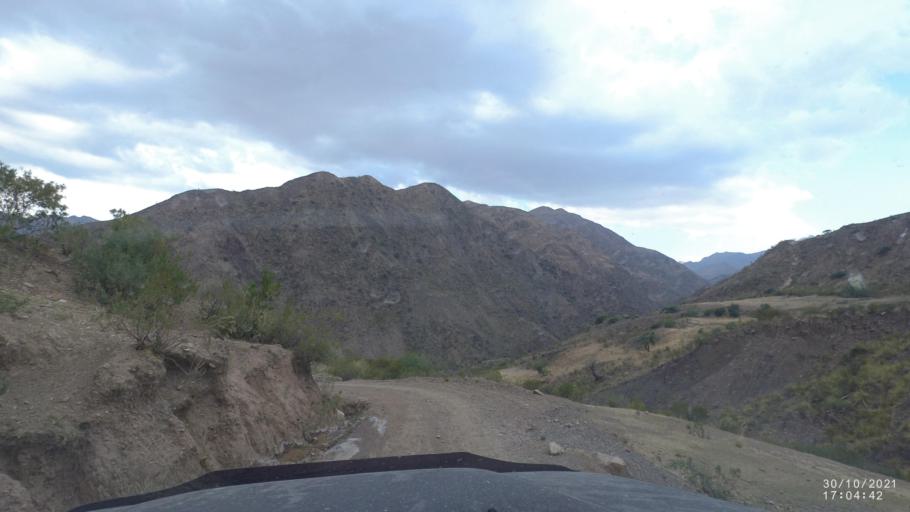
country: BO
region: Cochabamba
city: Colchani
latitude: -17.5677
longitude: -66.6301
